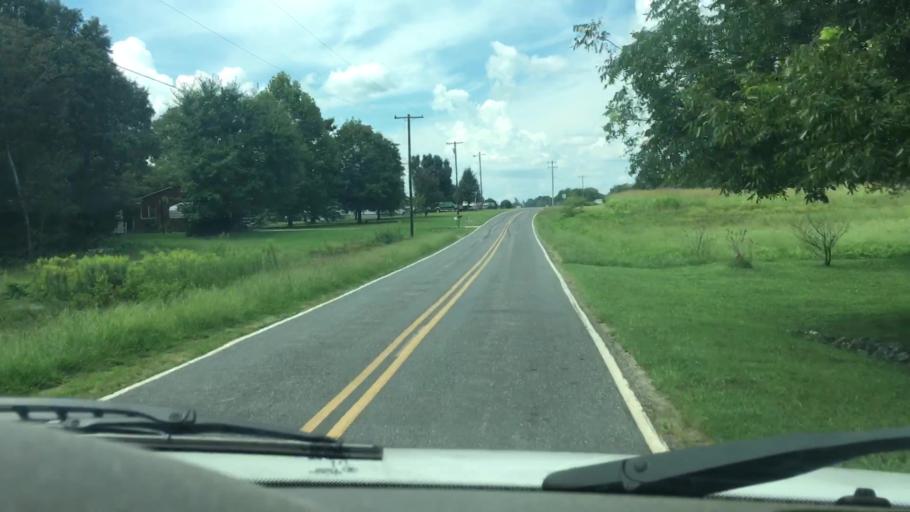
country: US
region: North Carolina
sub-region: Iredell County
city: Troutman
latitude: 35.6764
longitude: -80.8451
